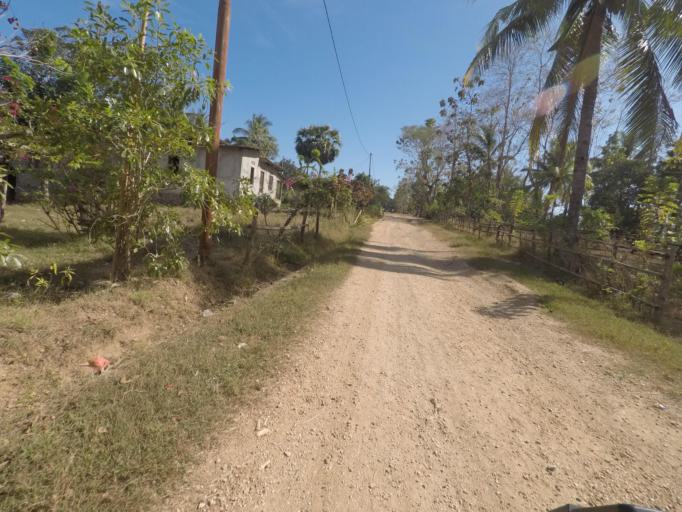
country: TL
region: Bobonaro
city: Maliana
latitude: -8.9560
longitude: 125.2179
